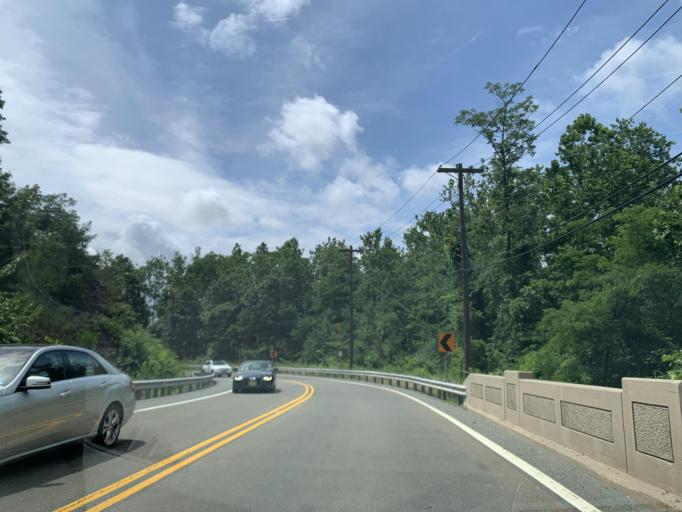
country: US
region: New Jersey
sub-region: Somerset County
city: Martinsville
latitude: 40.5850
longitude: -74.5608
